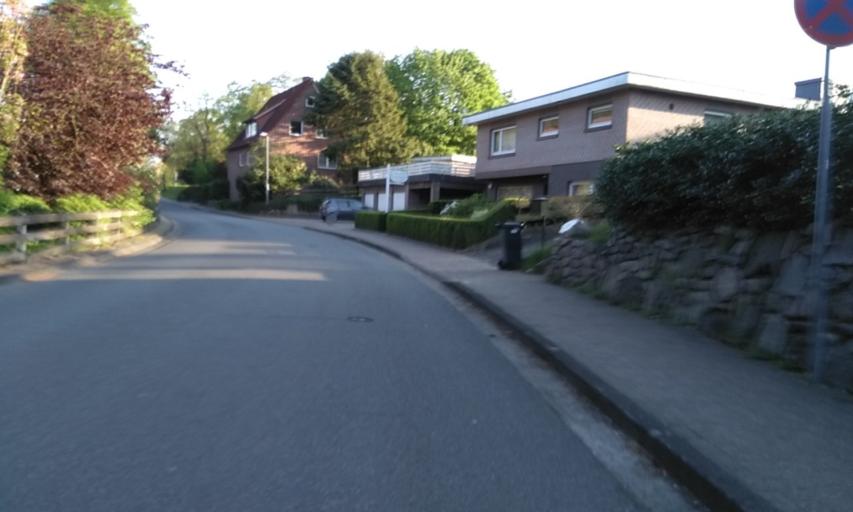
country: DE
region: Lower Saxony
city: Dollern
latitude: 53.5379
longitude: 9.5480
